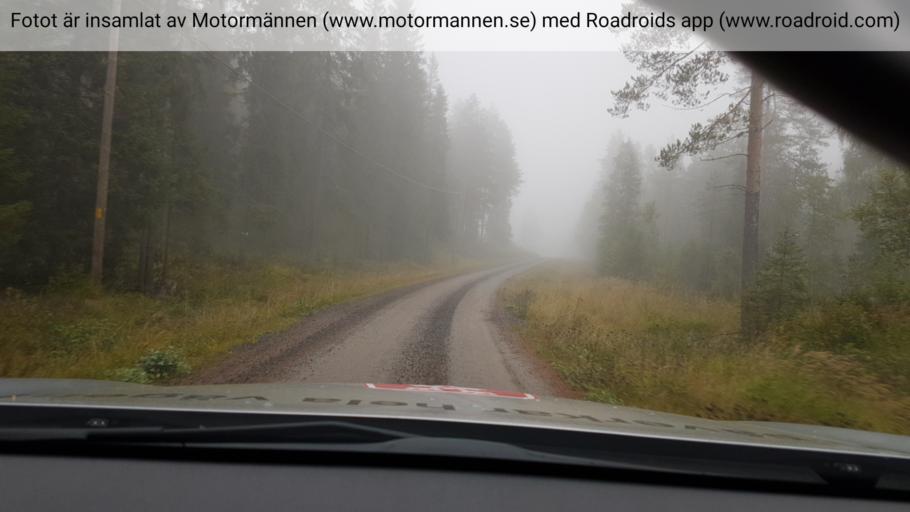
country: SE
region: Vaesterbotten
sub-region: Skelleftea Kommun
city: Burtraesk
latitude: 64.2959
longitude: 20.4060
